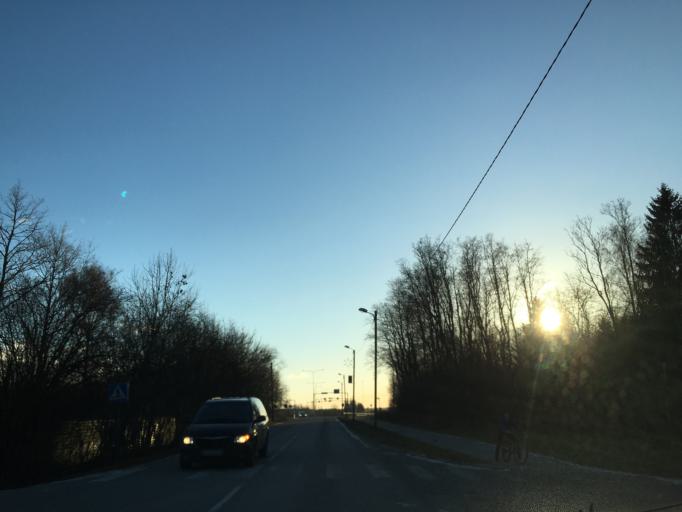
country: EE
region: Harju
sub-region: Saue linn
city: Saue
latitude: 59.3142
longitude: 24.5605
